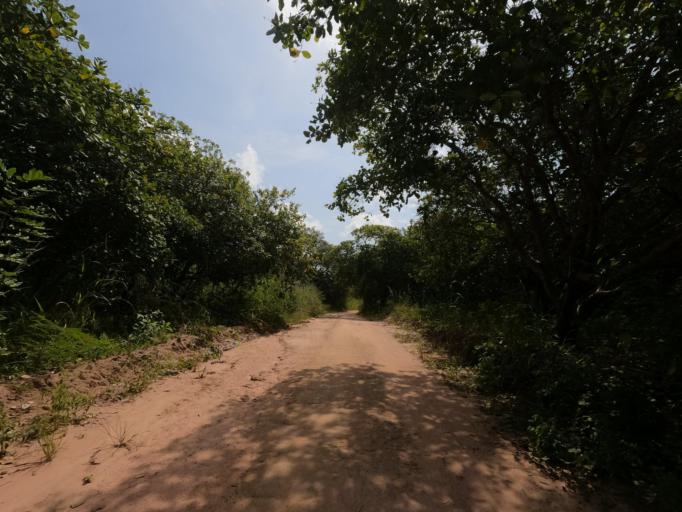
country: GW
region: Oio
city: Bissora
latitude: 12.4011
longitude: -15.7224
